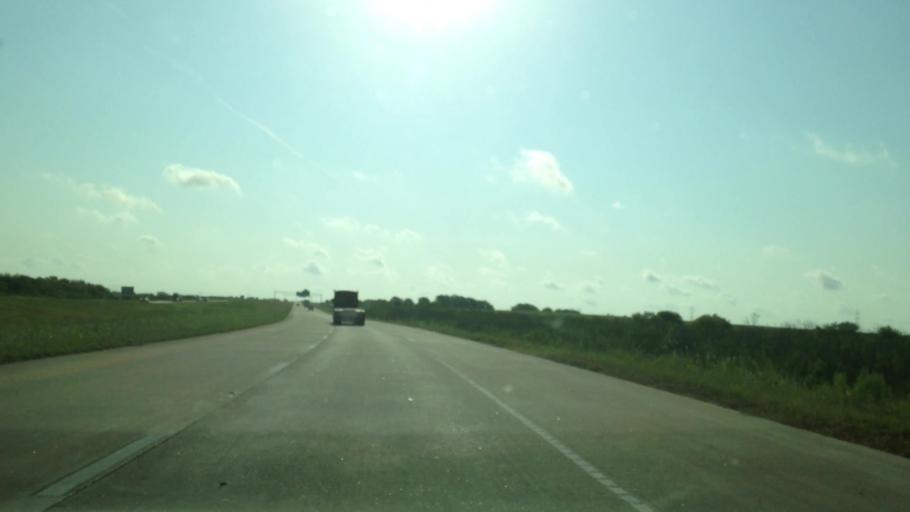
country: US
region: Texas
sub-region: Travis County
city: Onion Creek
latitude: 30.0807
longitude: -97.7255
